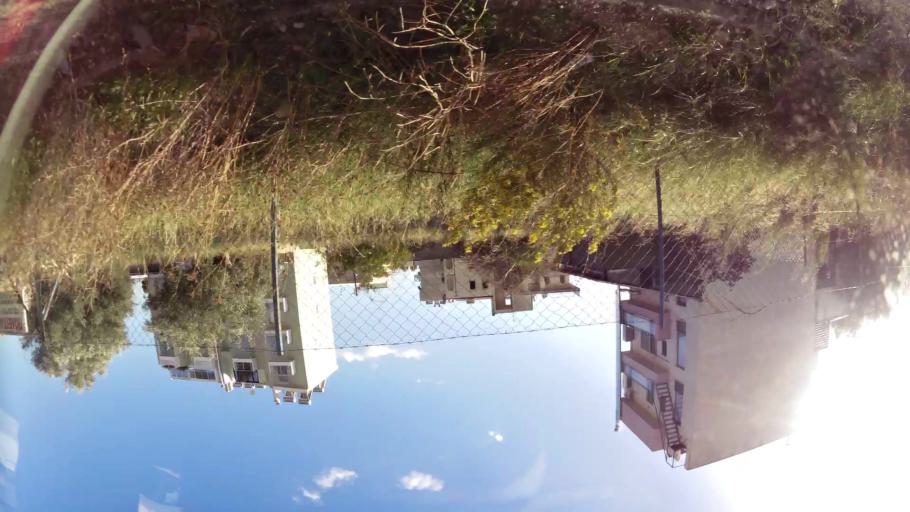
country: GR
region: Attica
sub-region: Nomarchia Anatolikis Attikis
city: Acharnes
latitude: 38.0681
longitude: 23.7400
